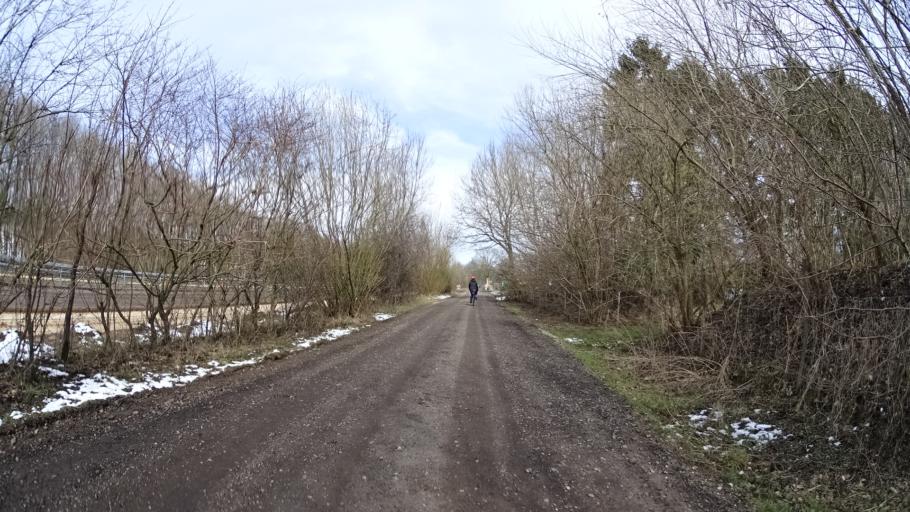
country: DE
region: Schleswig-Holstein
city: Wankendorf
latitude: 54.1156
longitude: 10.2166
